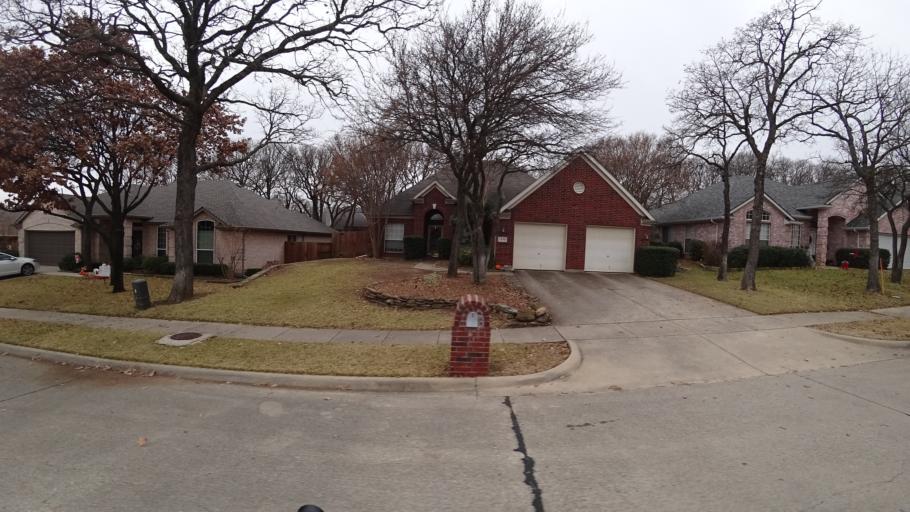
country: US
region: Texas
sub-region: Denton County
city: Lewisville
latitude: 33.0300
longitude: -97.0298
